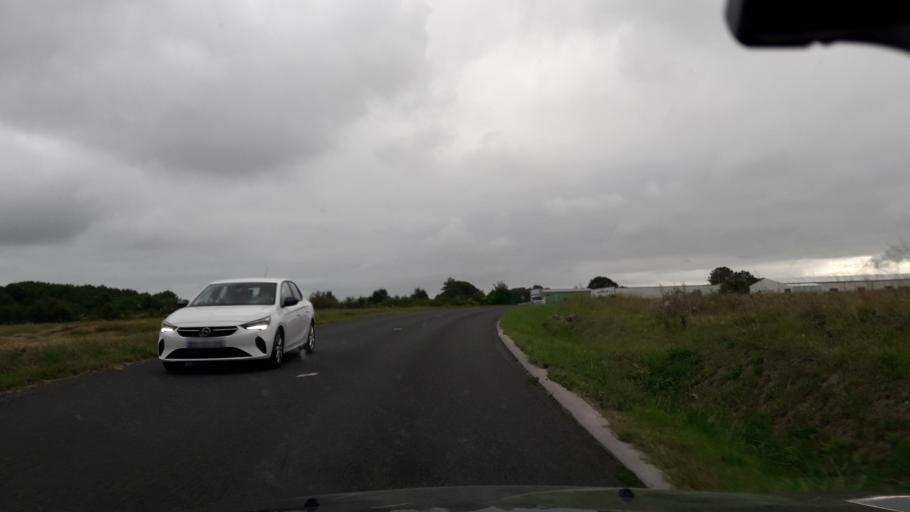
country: FR
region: Poitou-Charentes
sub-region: Departement de la Charente-Maritime
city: Arvert
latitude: 45.7277
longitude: -1.1378
